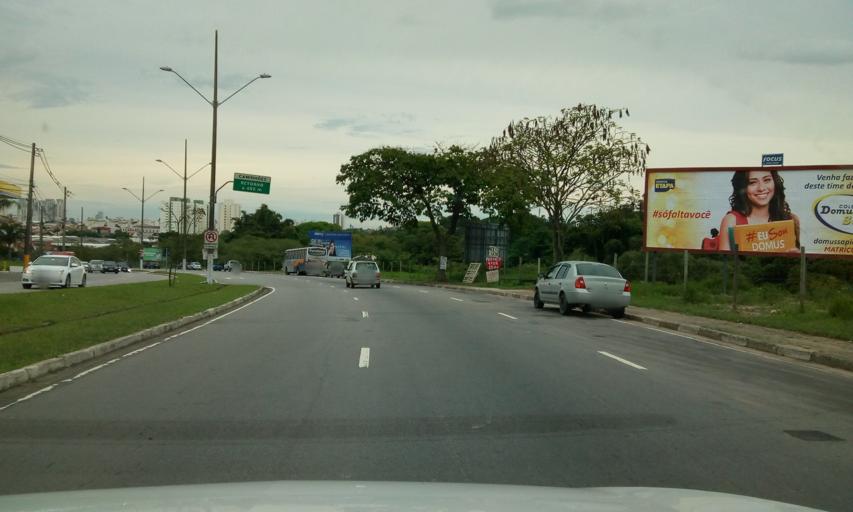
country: BR
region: Sao Paulo
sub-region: Jundiai
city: Jundiai
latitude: -23.2260
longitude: -46.8734
